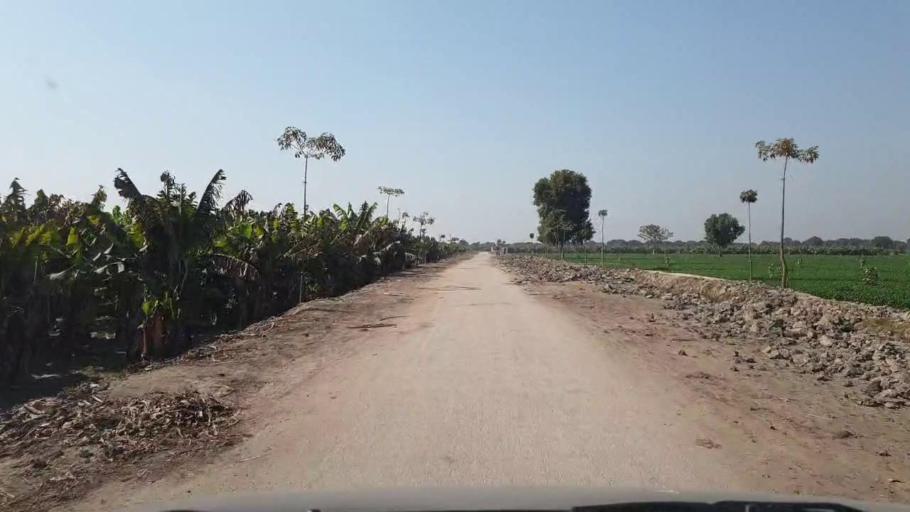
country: PK
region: Sindh
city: Tando Jam
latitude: 25.4136
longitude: 68.6295
